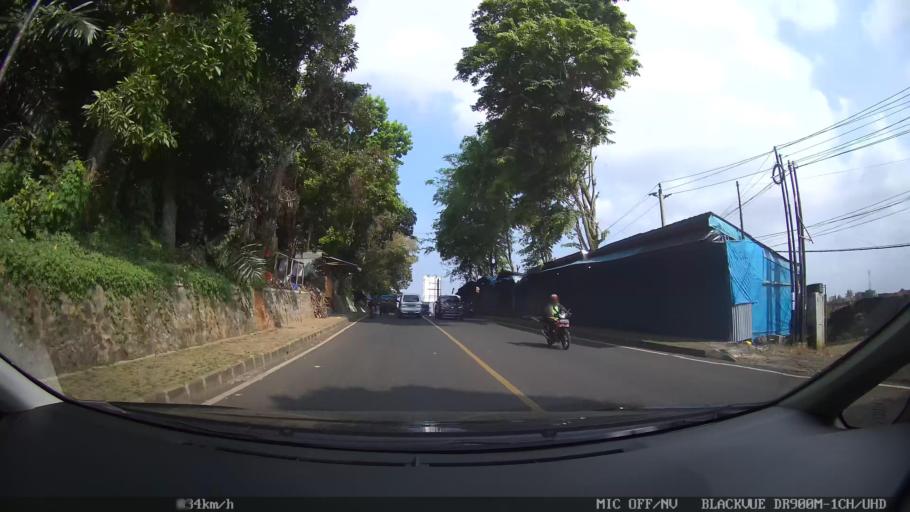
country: ID
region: Lampung
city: Kedaton
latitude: -5.3984
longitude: 105.2427
